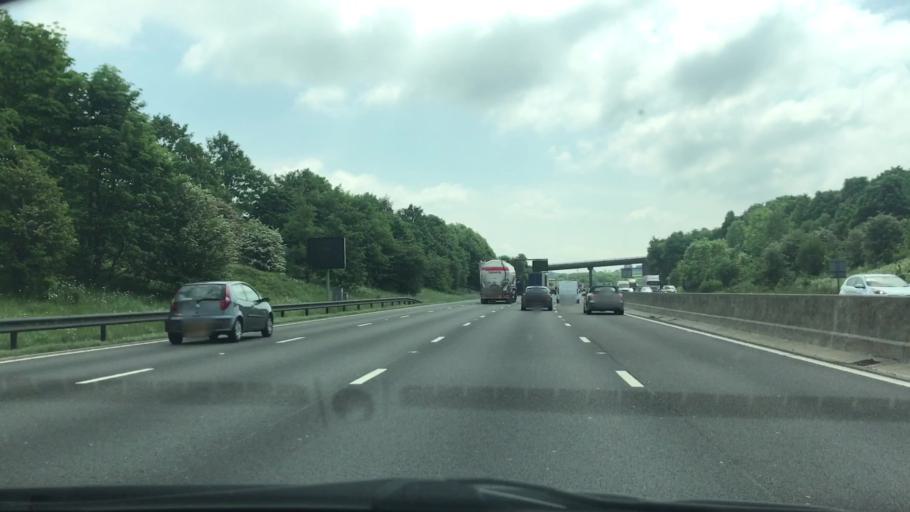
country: GB
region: England
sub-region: Derbyshire
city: Tibshelf
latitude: 53.1675
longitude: -1.3241
